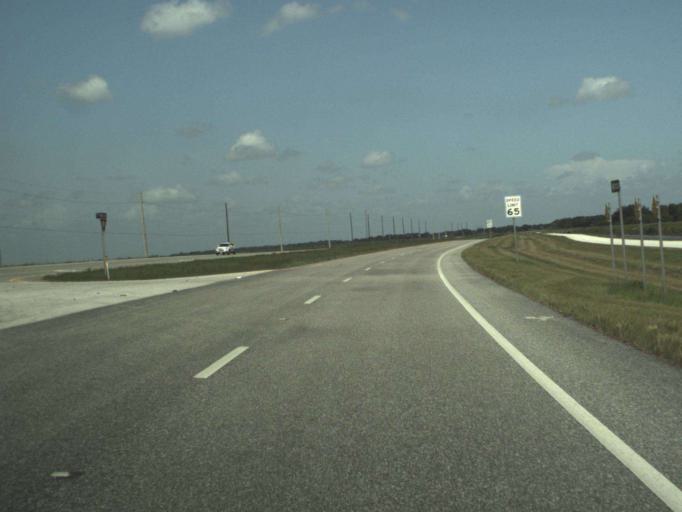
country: US
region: Florida
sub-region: Saint Lucie County
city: Fort Pierce South
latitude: 27.3694
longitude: -80.5579
